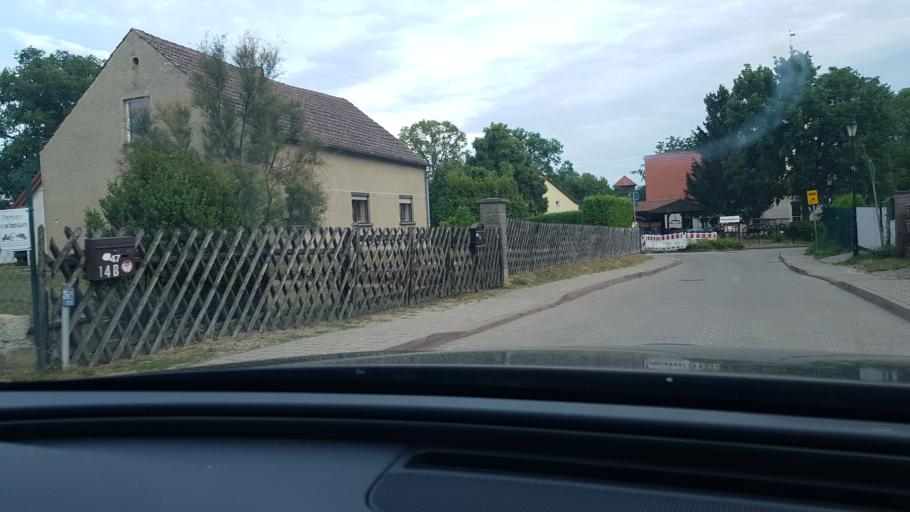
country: DE
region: Brandenburg
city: Grossbeeren
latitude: 52.3404
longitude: 13.3539
